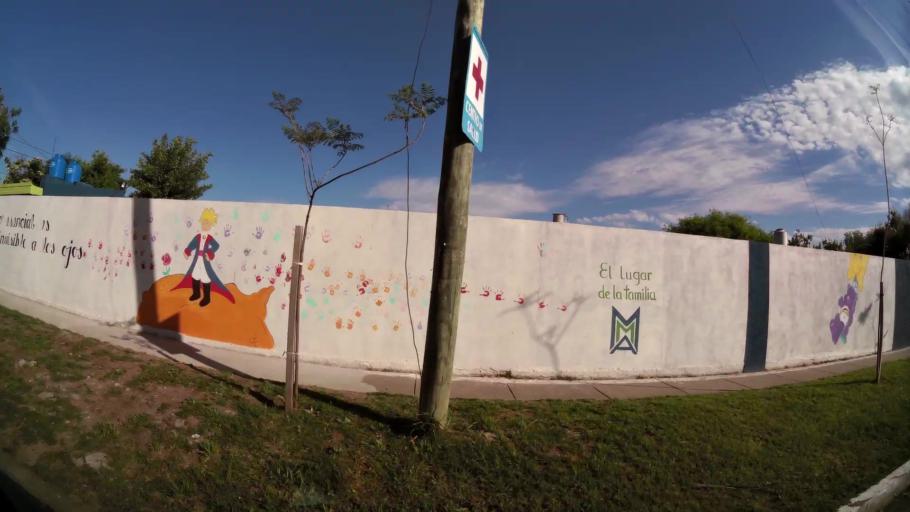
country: AR
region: Buenos Aires
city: Santa Catalina - Dique Lujan
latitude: -34.4907
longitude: -58.7102
